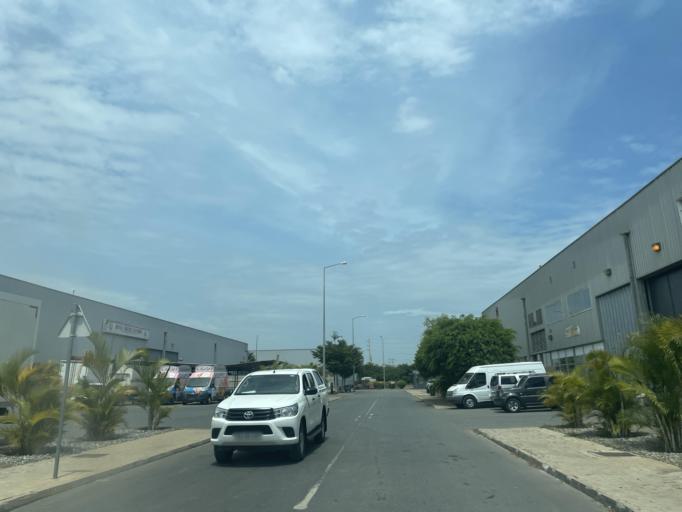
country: AO
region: Luanda
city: Luanda
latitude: -8.9606
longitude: 13.3908
